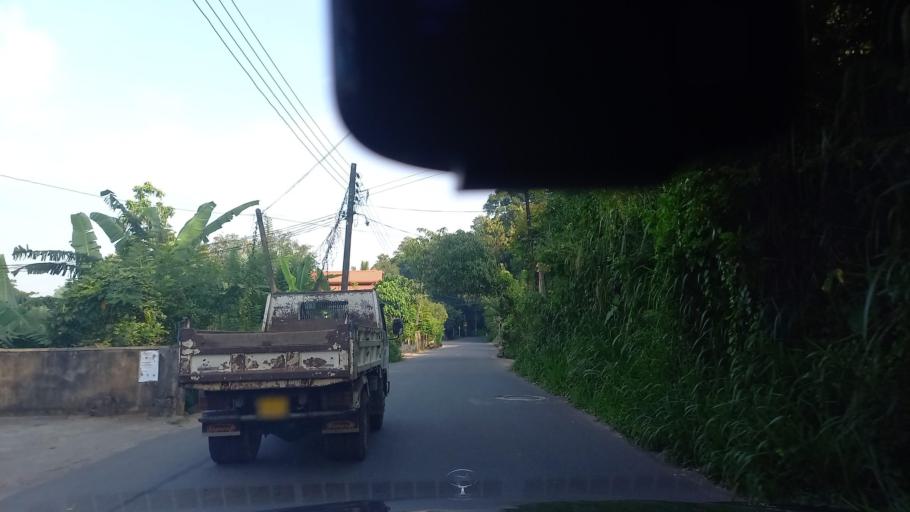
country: LK
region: Central
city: Kandy
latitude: 7.2395
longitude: 80.6005
